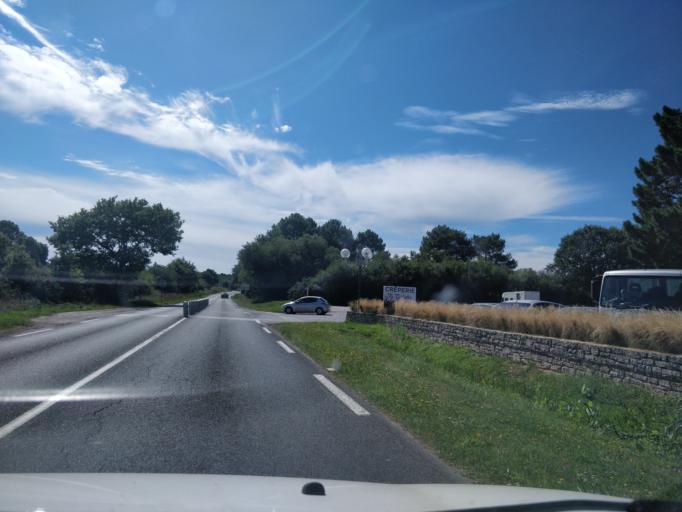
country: FR
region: Brittany
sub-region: Departement du Morbihan
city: Saint-Philibert
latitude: 47.6019
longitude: -2.9926
